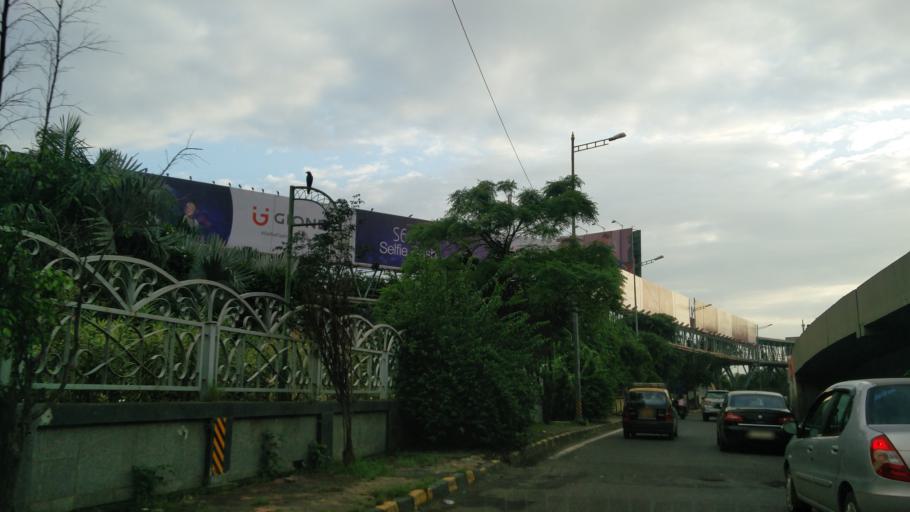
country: IN
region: Maharashtra
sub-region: Mumbai Suburban
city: Mumbai
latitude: 19.0534
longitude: 72.8461
